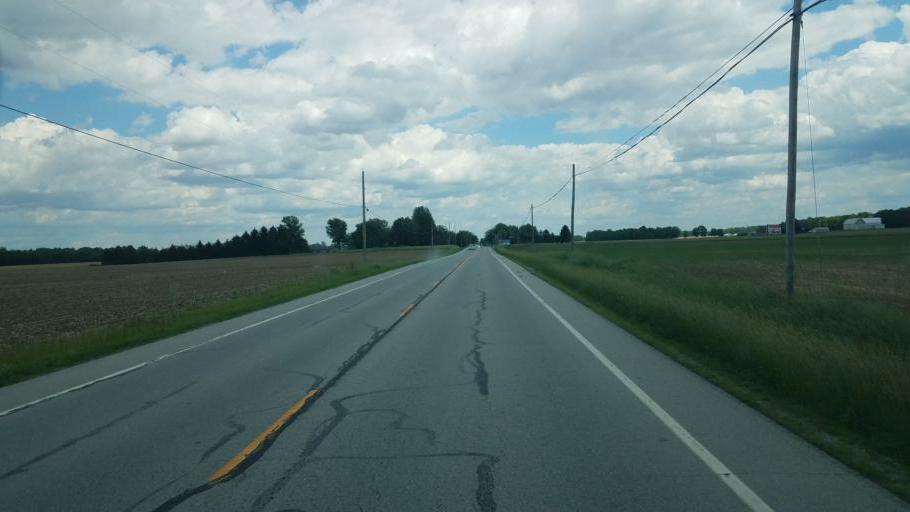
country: US
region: Ohio
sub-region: Crawford County
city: Bucyrus
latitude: 40.8129
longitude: -82.8906
